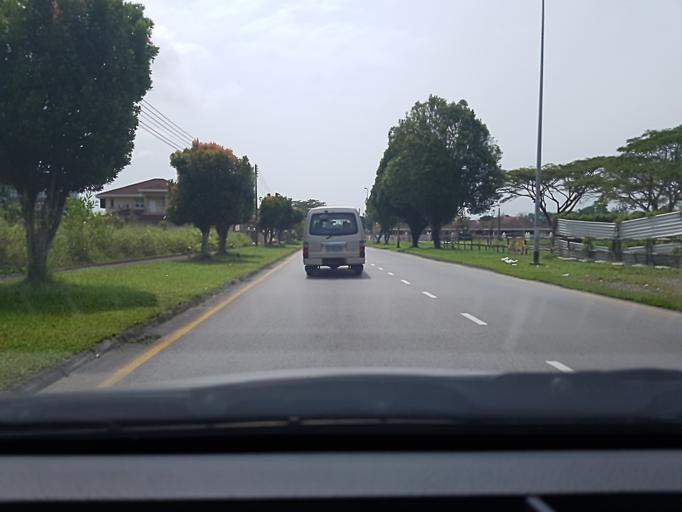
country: MY
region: Sarawak
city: Kuching
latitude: 1.5211
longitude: 110.3693
